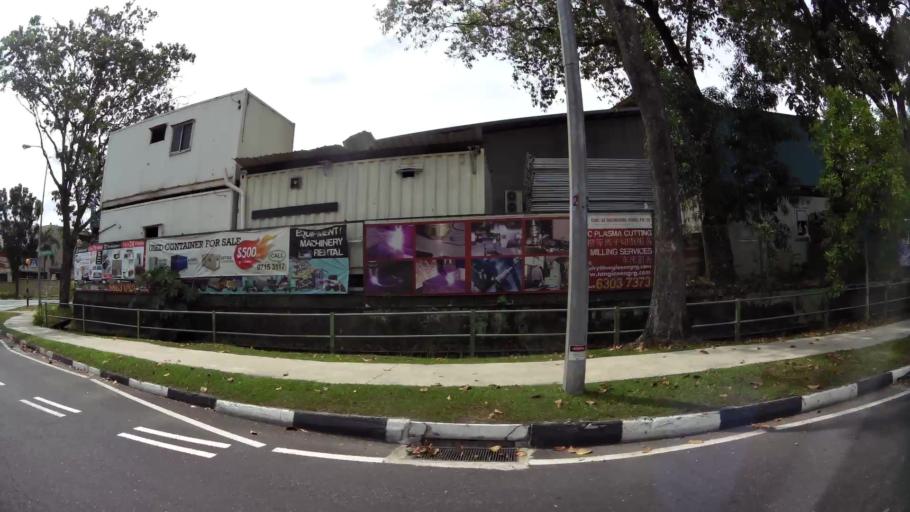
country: MY
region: Johor
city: Johor Bahru
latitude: 1.4087
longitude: 103.7524
